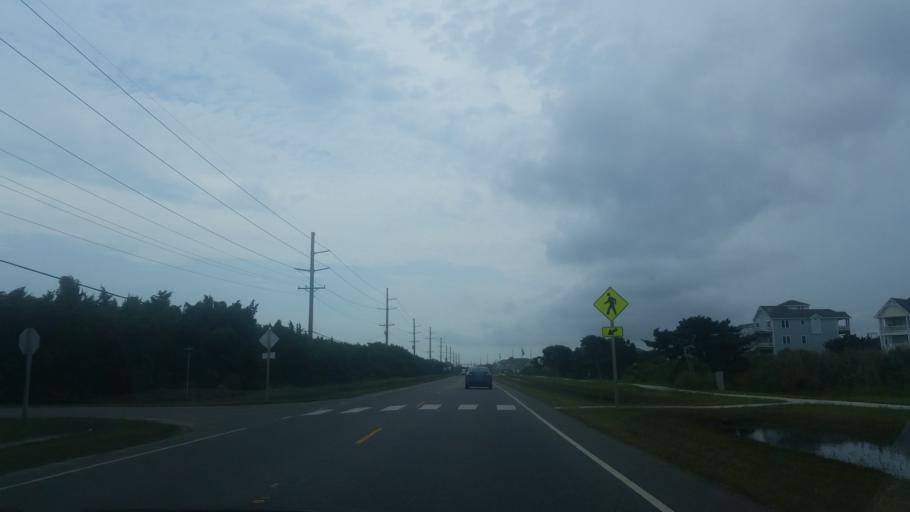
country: US
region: North Carolina
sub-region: Dare County
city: Buxton
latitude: 35.3385
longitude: -75.5055
